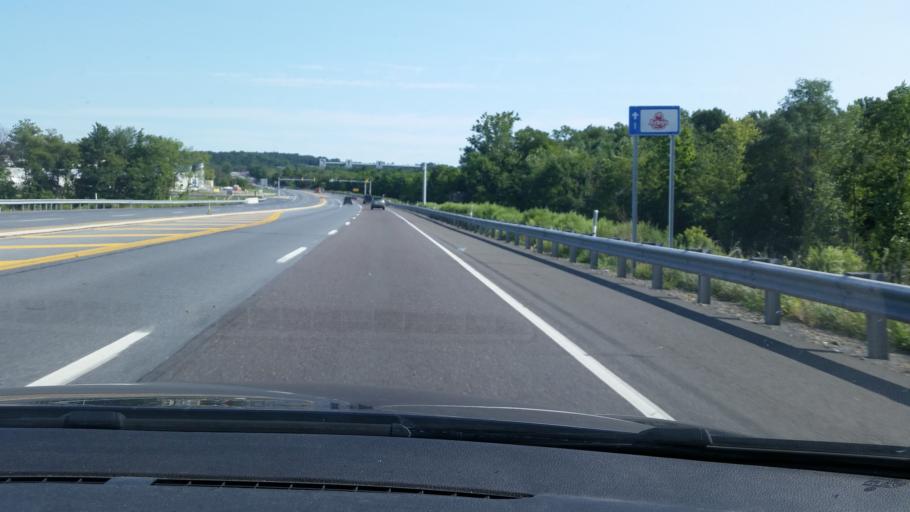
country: US
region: Pennsylvania
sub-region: Berks County
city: Hamburg
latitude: 40.5503
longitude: -75.9906
